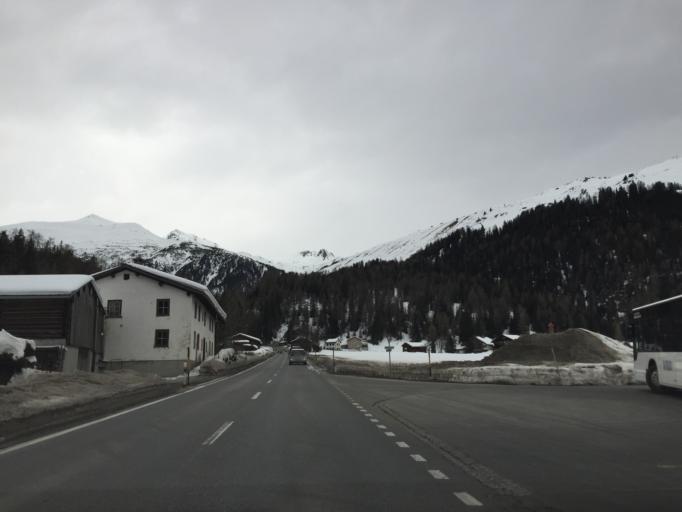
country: CH
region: Grisons
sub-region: Praettigau/Davos District
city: Davos
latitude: 46.8396
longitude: 9.8708
